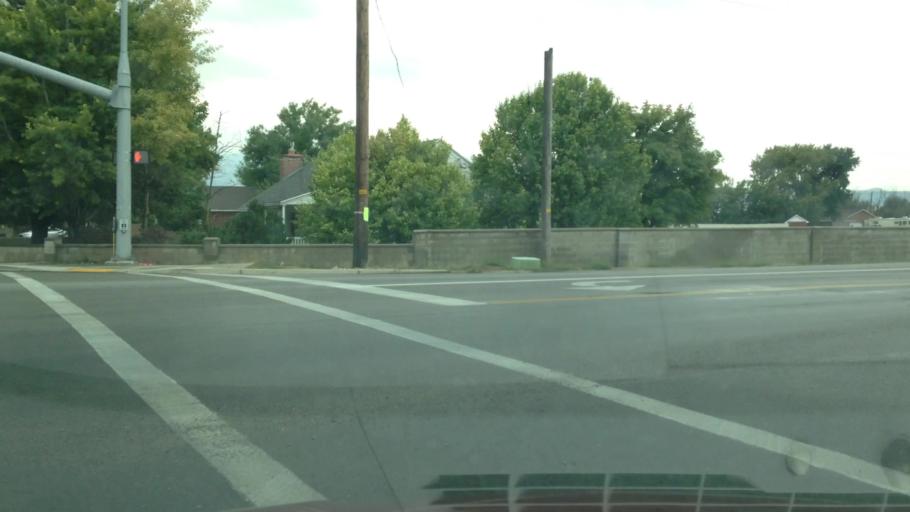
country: US
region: Utah
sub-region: Utah County
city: Lehi
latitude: 40.3874
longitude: -111.8865
